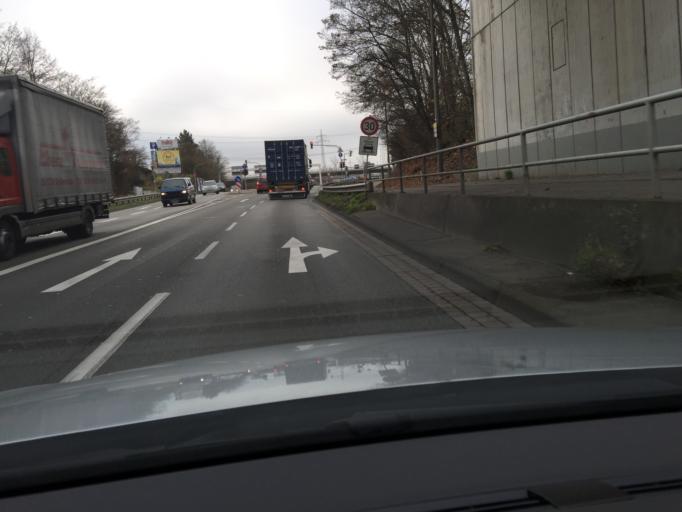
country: DE
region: Rheinland-Pfalz
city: Sankt Sebastian
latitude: 50.3875
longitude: 7.5642
